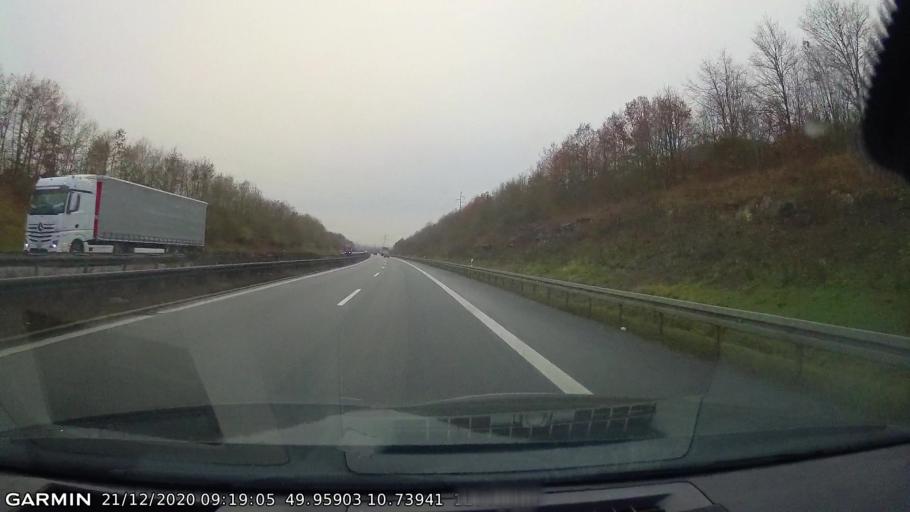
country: DE
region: Bavaria
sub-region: Regierungsbezirk Unterfranken
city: Stettfeld
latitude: 49.9590
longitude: 10.7397
